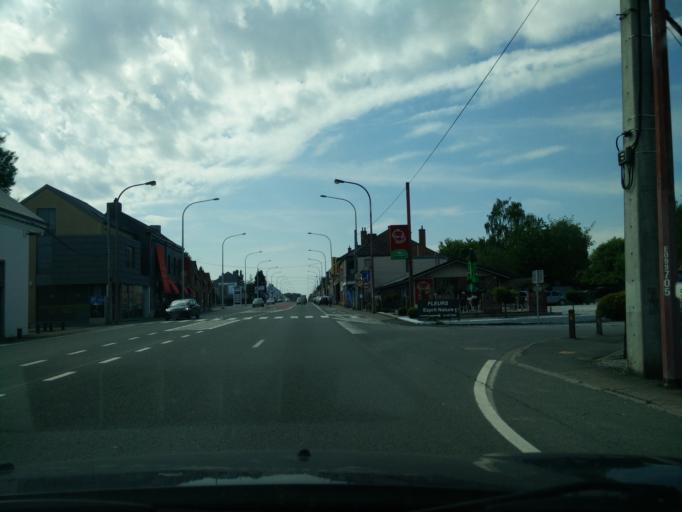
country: BE
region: Wallonia
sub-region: Province du Hainaut
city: Gerpinnes
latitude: 50.3424
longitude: 4.4734
